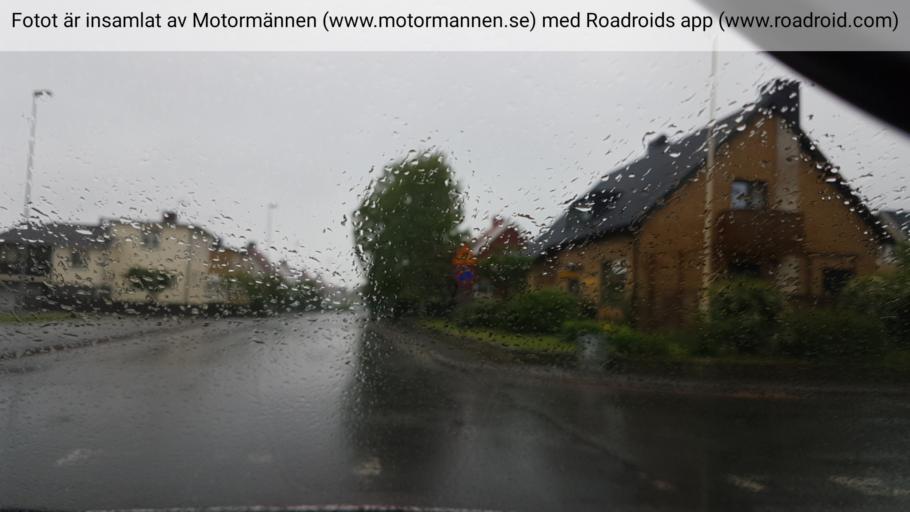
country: SE
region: Vaestra Goetaland
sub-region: Falkopings Kommun
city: Falkoeping
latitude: 58.1666
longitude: 13.5610
